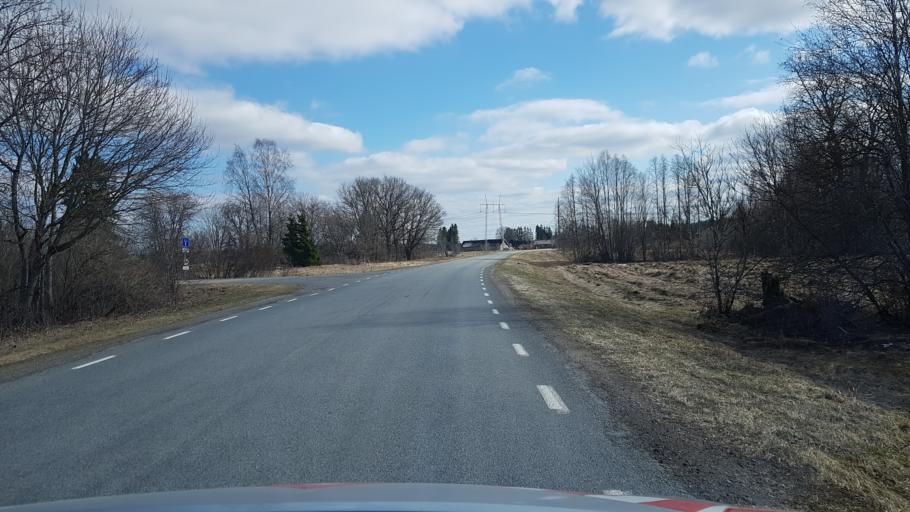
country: EE
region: Laeaene-Virumaa
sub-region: Tamsalu vald
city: Tamsalu
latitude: 59.1812
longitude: 26.0492
